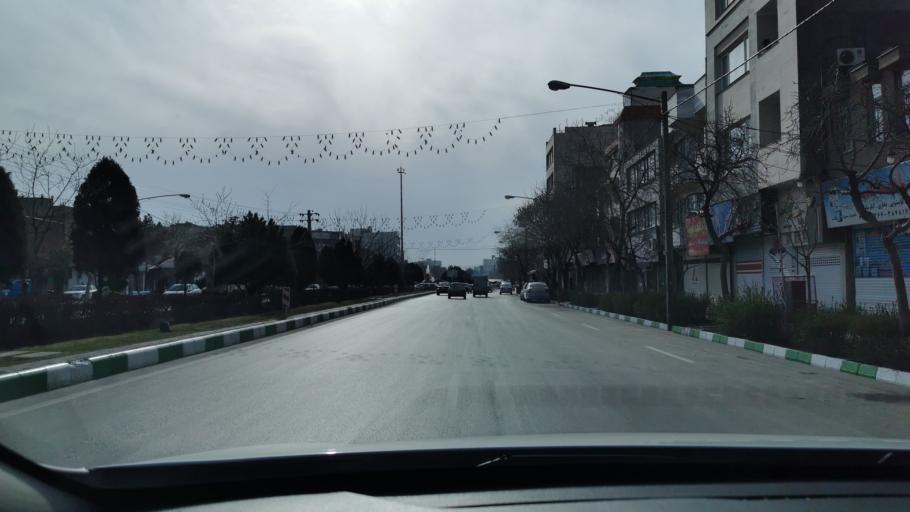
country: IR
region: Razavi Khorasan
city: Mashhad
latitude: 36.2967
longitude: 59.5280
